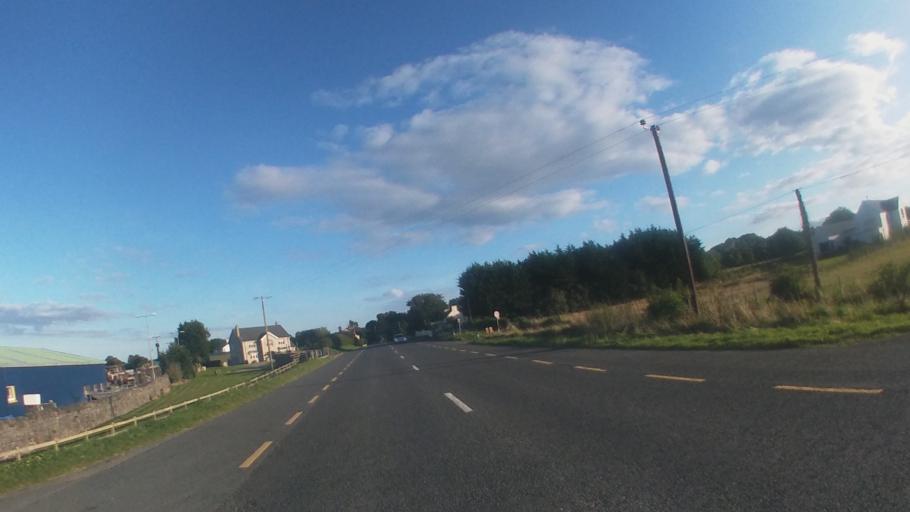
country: IE
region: Leinster
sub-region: Lu
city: Carlingford
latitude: 54.0297
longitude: -6.1571
